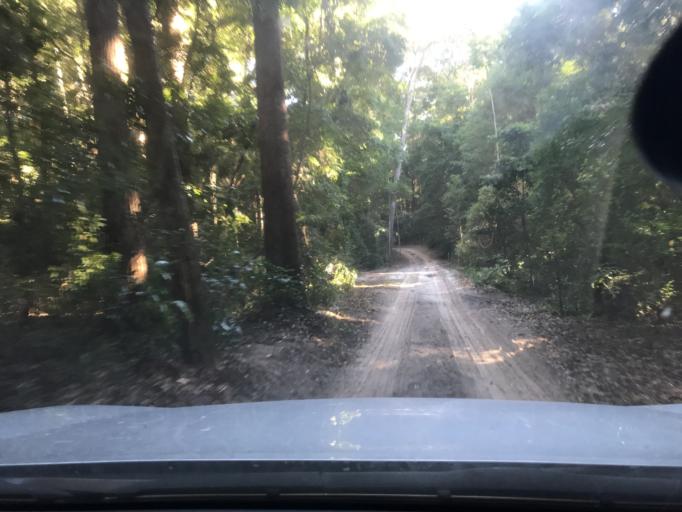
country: AU
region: Queensland
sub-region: Fraser Coast
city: Urangan
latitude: -25.3249
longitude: 153.1513
